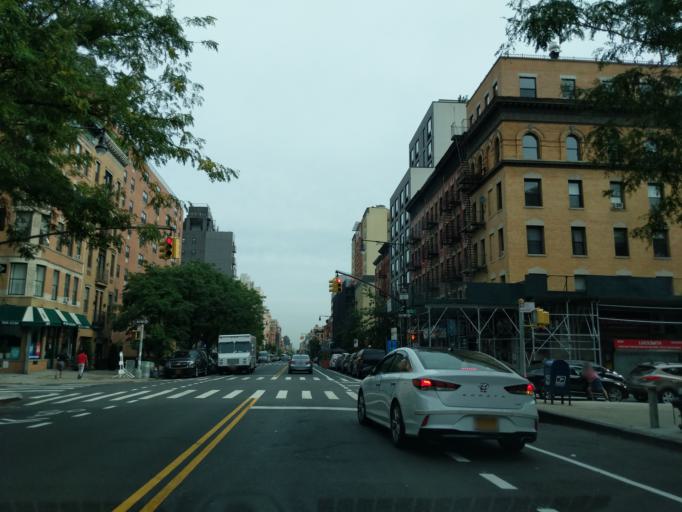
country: US
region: New York
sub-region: New York County
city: Manhattan
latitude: 40.8015
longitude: -73.9575
